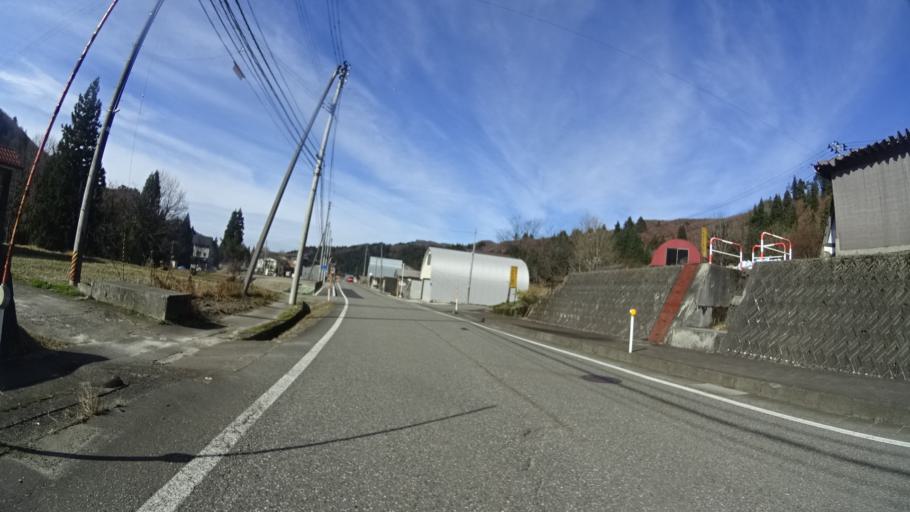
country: JP
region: Niigata
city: Muikamachi
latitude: 37.2030
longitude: 139.0742
